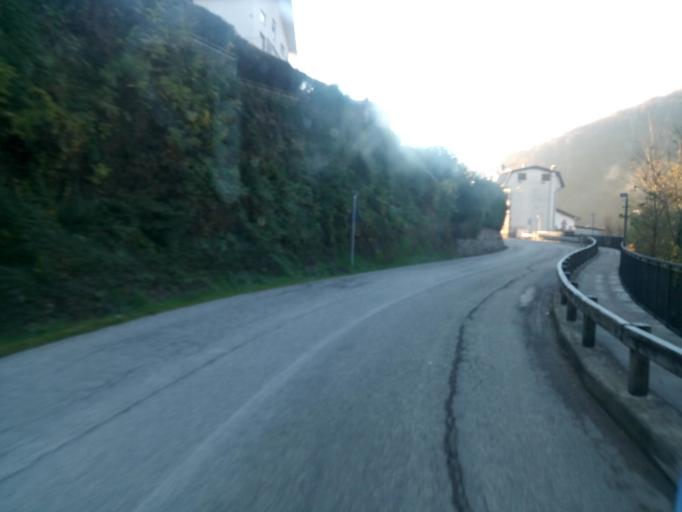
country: IT
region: Veneto
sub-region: Provincia di Vicenza
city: Valli del Pasubio
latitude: 45.7387
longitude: 11.2656
